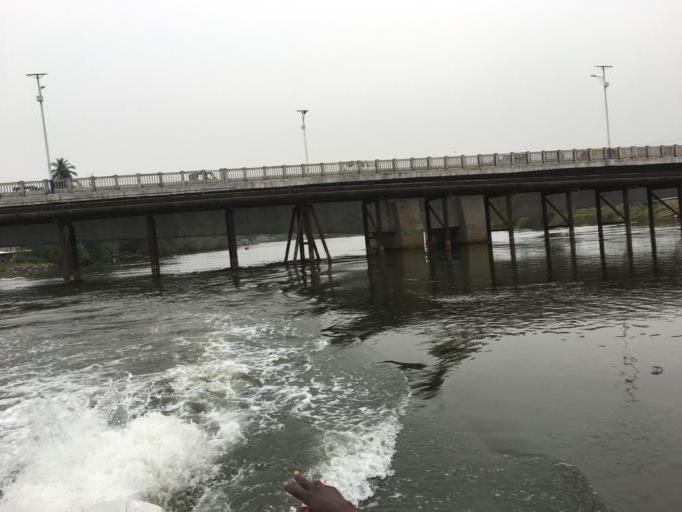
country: LR
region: Montserrado
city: Monrovia
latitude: 6.3726
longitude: -10.7793
